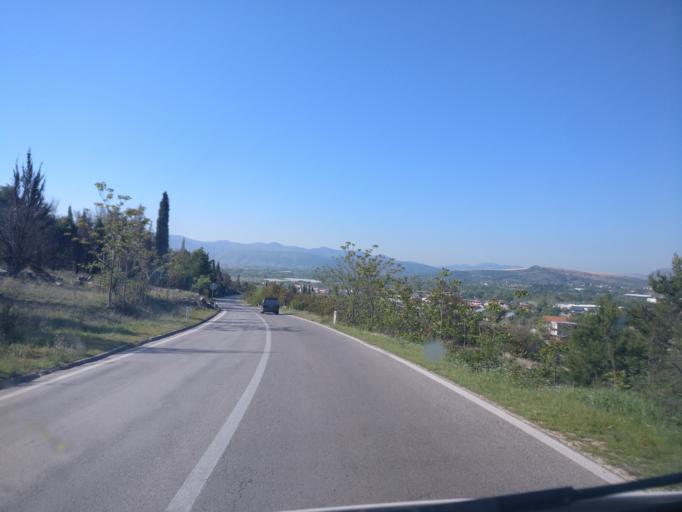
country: BA
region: Federation of Bosnia and Herzegovina
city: Tasovcici
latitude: 43.1178
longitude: 17.7226
